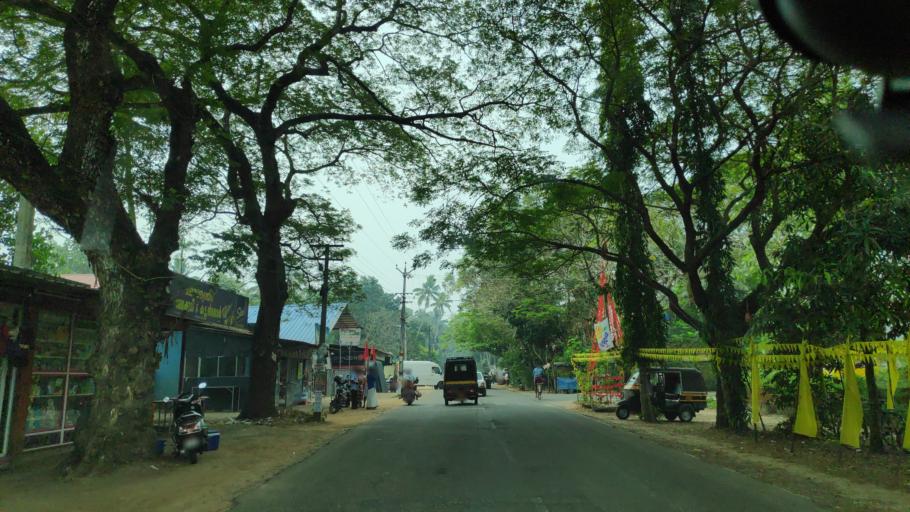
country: IN
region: Kerala
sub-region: Alappuzha
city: Shertallai
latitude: 9.5856
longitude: 76.3517
